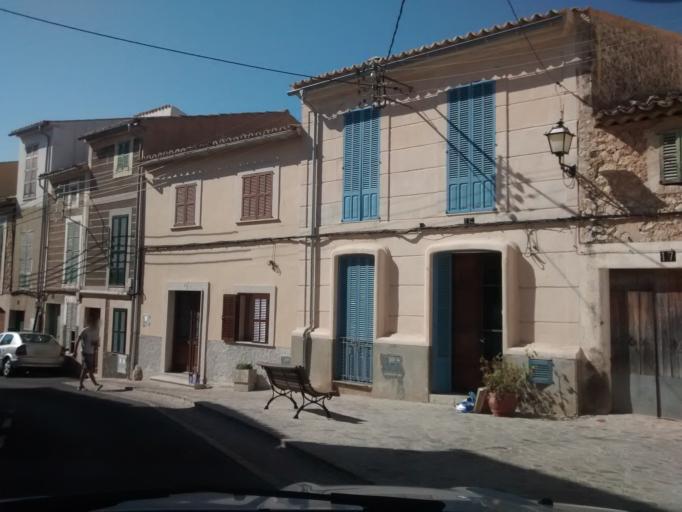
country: ES
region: Balearic Islands
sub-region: Illes Balears
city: Alaro
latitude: 39.7052
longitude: 2.7864
